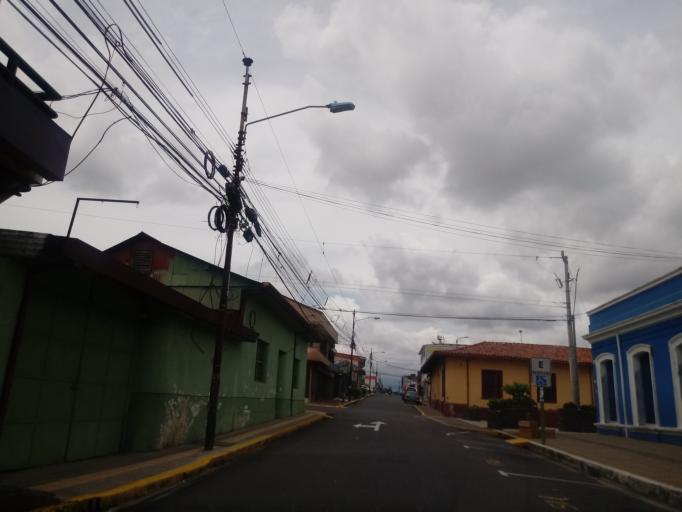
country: CR
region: Heredia
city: Heredia
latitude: 9.9998
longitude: -84.1179
